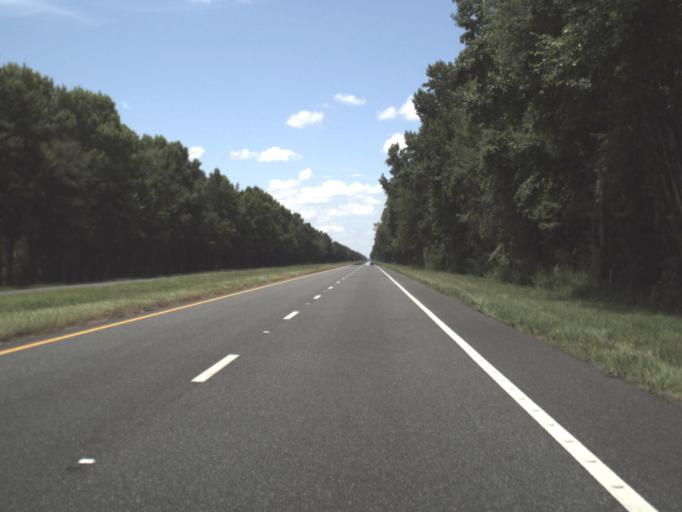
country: US
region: Florida
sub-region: Taylor County
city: Perry
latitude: 30.2429
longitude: -83.6932
